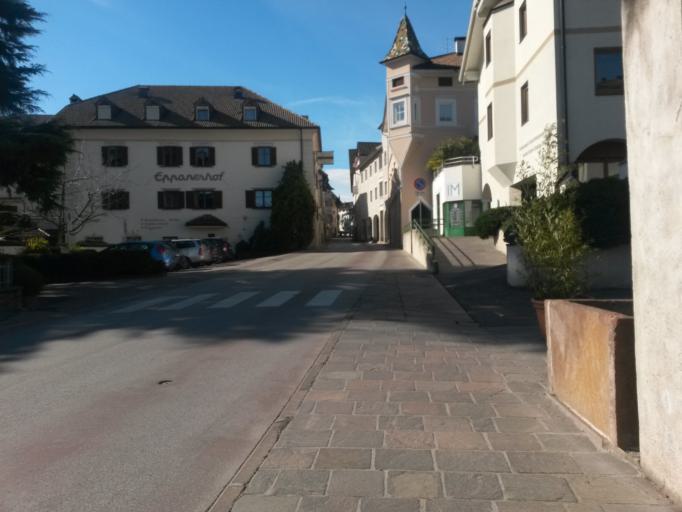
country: IT
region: Trentino-Alto Adige
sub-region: Bolzano
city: San Michele
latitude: 46.4577
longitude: 11.2592
